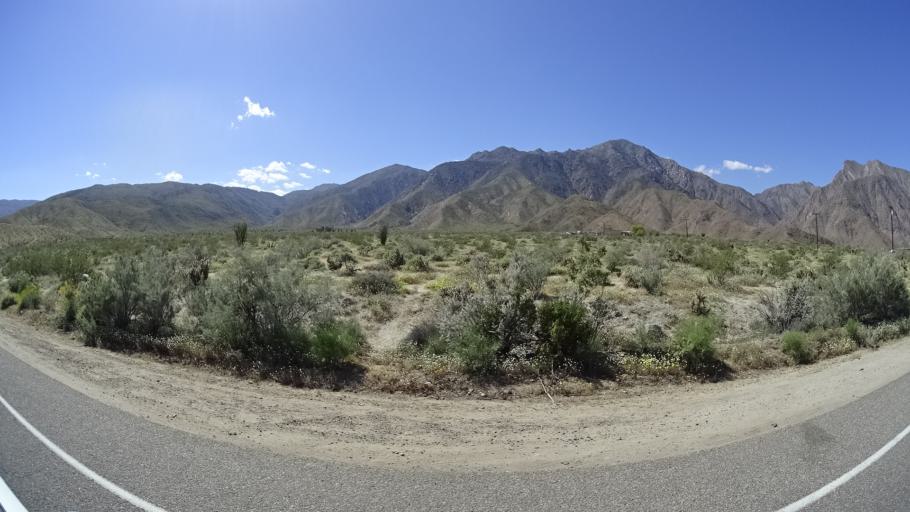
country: US
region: California
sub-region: San Diego County
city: Borrego Springs
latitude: 33.2550
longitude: -116.3993
